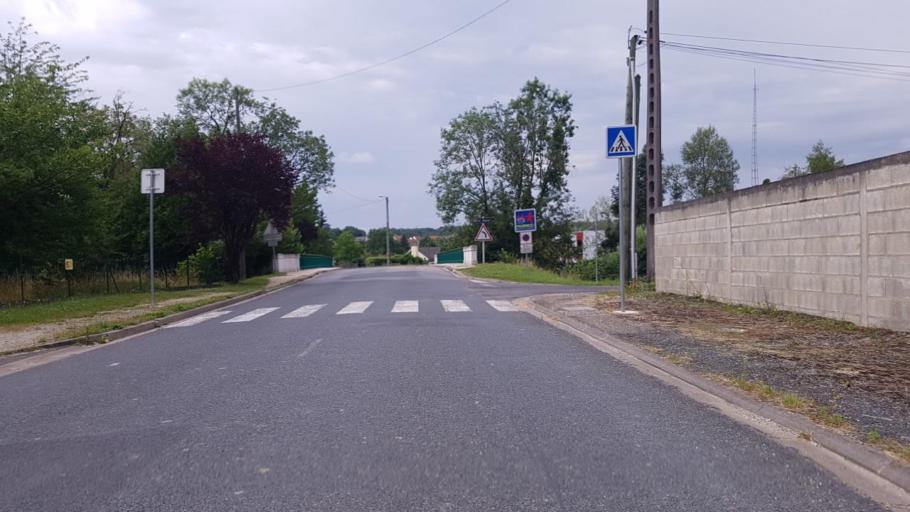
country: FR
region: Champagne-Ardenne
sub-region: Departement de la Marne
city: Sermaize-les-Bains
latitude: 48.7882
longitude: 4.9057
